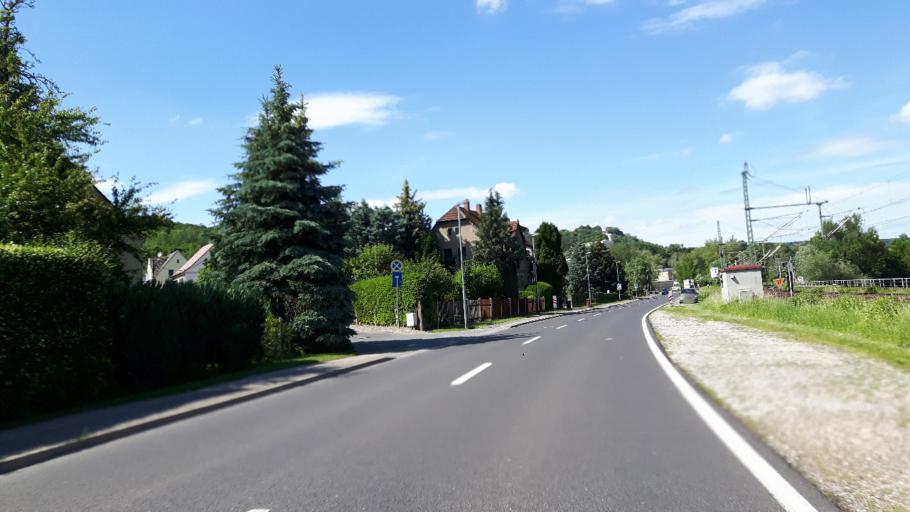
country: DE
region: Saxony-Anhalt
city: Bad Kosen
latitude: 51.1209
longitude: 11.7133
